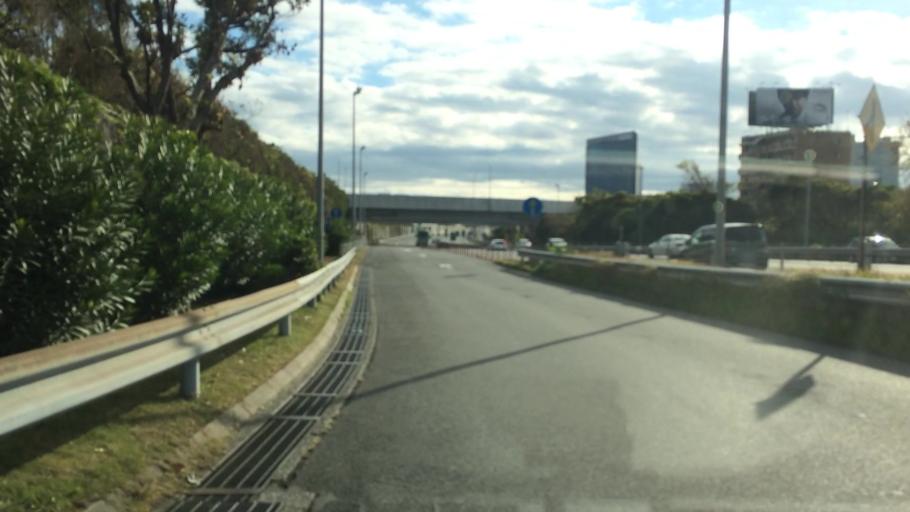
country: JP
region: Chiba
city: Funabashi
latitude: 35.6598
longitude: 140.0311
